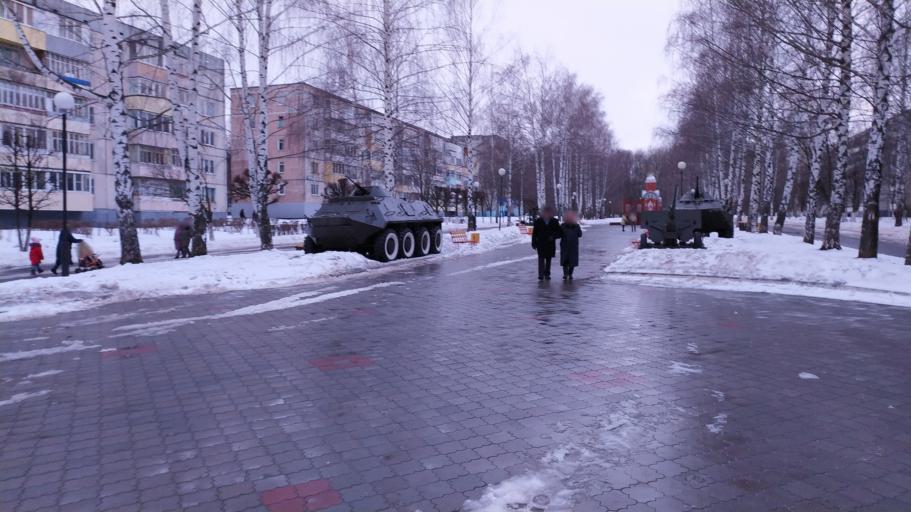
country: RU
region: Chuvashia
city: Novocheboksarsk
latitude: 56.1234
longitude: 47.4872
